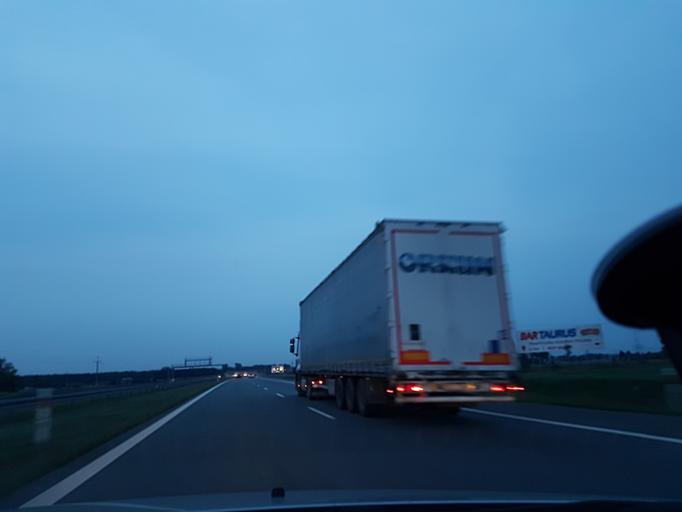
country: PL
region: Lodz Voivodeship
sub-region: Powiat kutnowski
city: Krzyzanow
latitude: 52.2087
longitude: 19.4813
